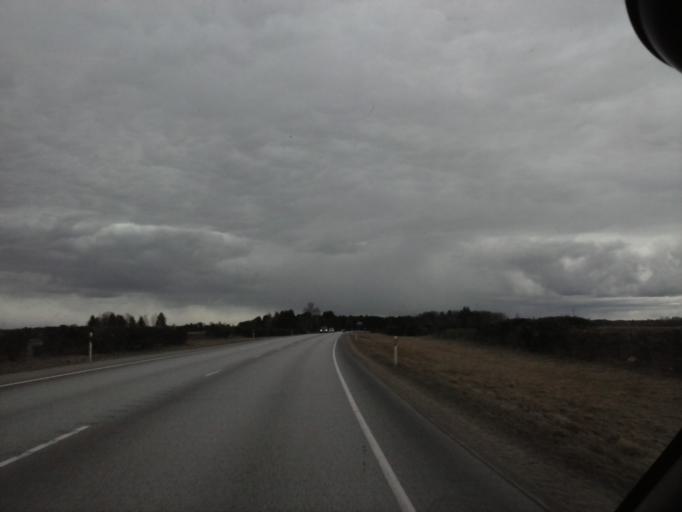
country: EE
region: Jaervamaa
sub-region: Paide linn
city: Paide
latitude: 58.8469
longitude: 25.7343
